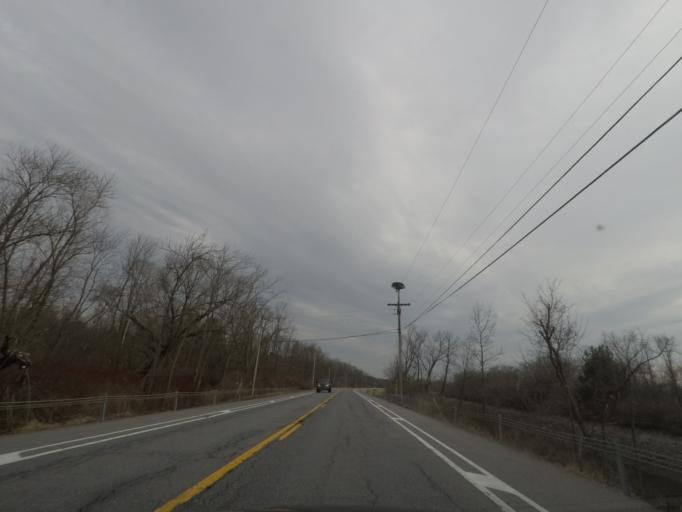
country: US
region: New York
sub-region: Washington County
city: Fort Edward
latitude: 43.1888
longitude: -73.5804
